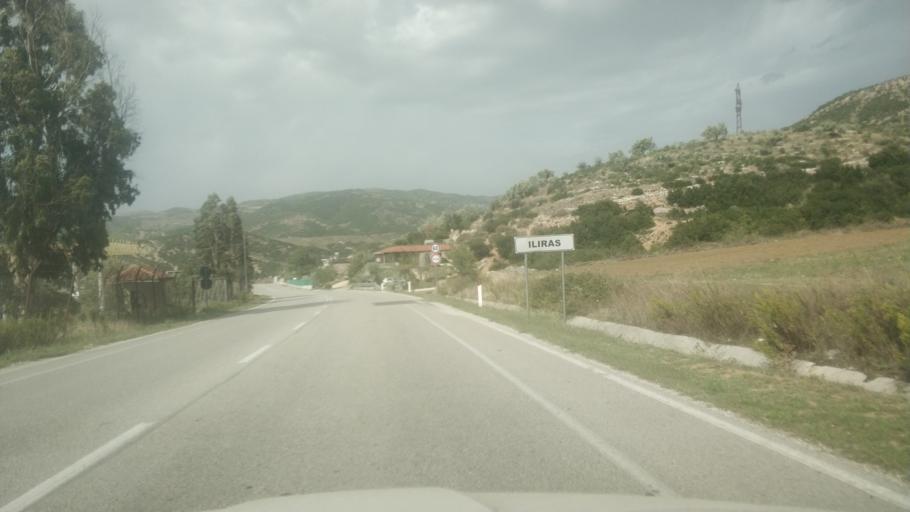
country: AL
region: Gjirokaster
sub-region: Rrethi i Tepelenes
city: Memaliaj
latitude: 40.3727
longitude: 19.9074
